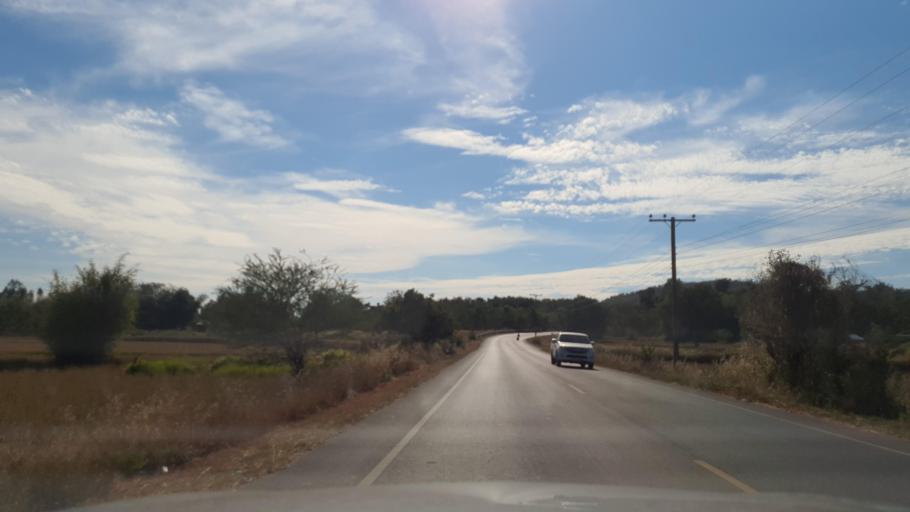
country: TH
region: Kalasin
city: Kuchinarai
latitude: 16.5861
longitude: 104.1268
